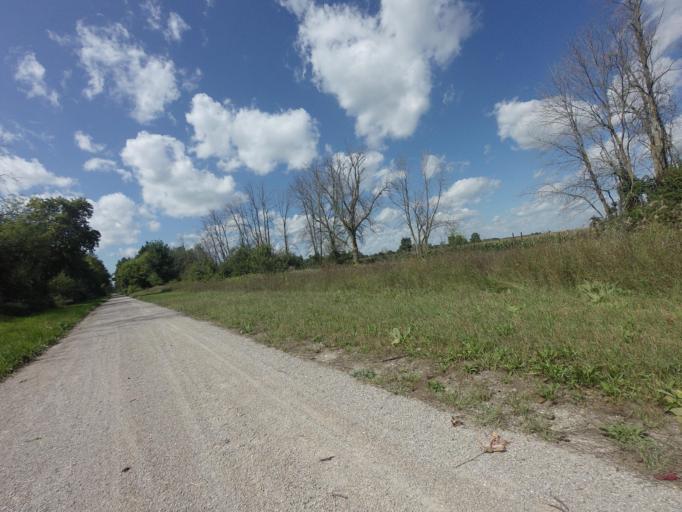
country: CA
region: Ontario
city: Huron East
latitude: 43.6816
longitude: -81.3028
